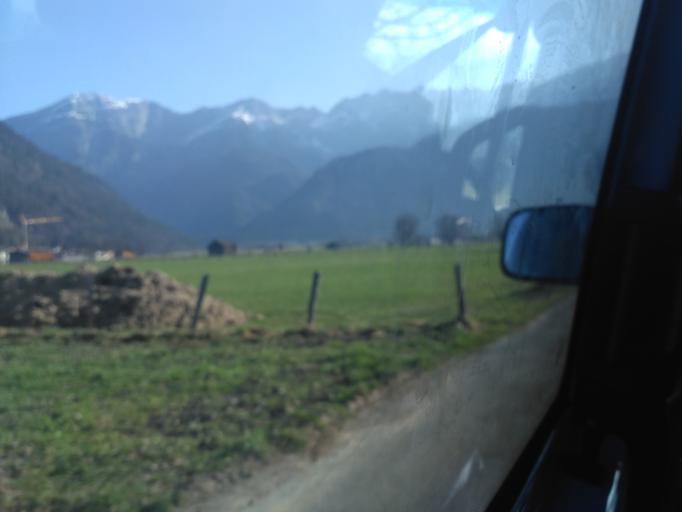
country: AT
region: Salzburg
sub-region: Politischer Bezirk Zell am See
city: Saalfelden am Steinernen Meer
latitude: 47.4471
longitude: 12.8086
